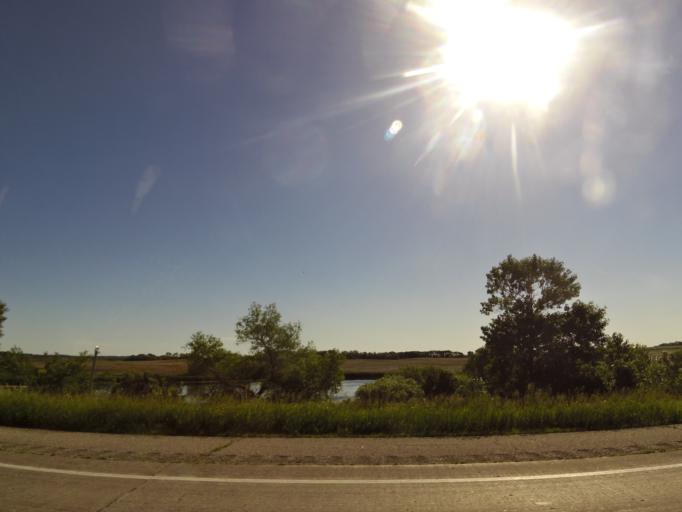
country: US
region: Minnesota
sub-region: Grant County
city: Elbow Lake
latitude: 46.0595
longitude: -95.8534
